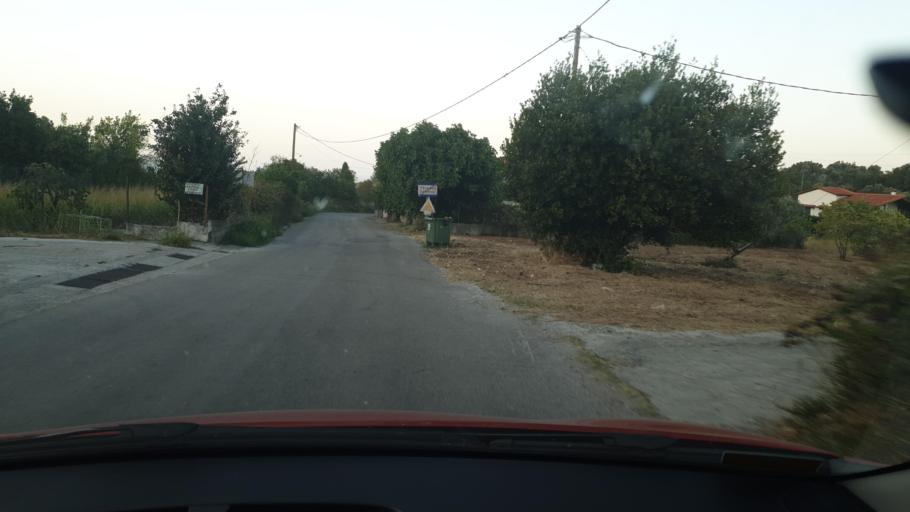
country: GR
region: Central Greece
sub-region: Nomos Evvoias
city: Oxilithos
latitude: 38.5876
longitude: 24.1140
